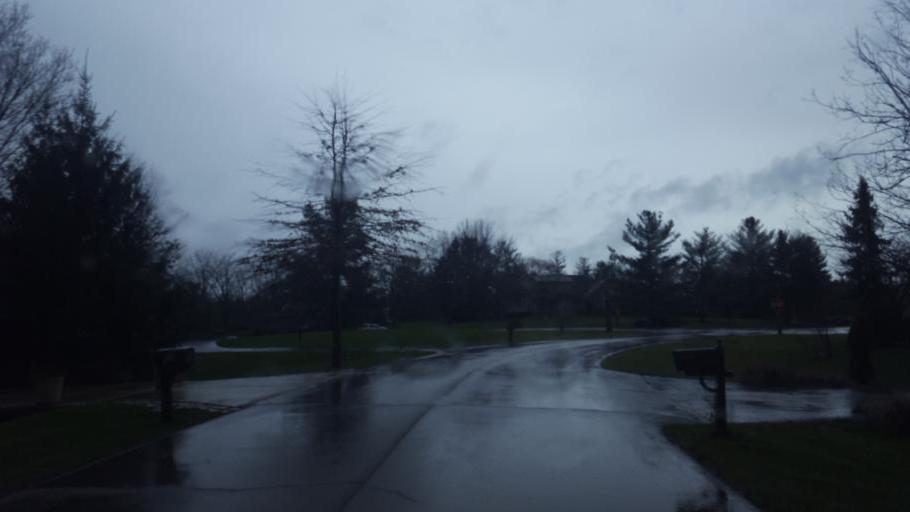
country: US
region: Ohio
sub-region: Delaware County
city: Powell
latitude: 40.1636
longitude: -83.0536
